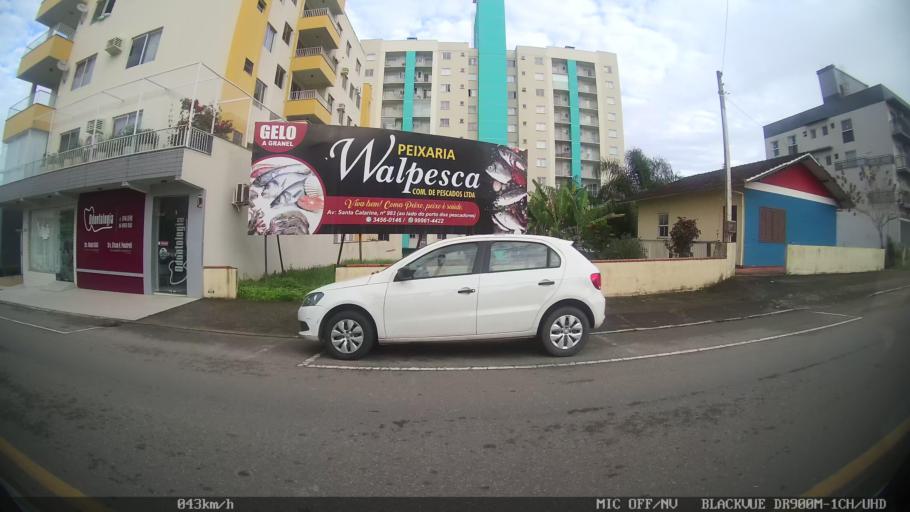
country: BR
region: Santa Catarina
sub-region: Barra Velha
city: Barra Velha
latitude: -26.6363
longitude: -48.6851
